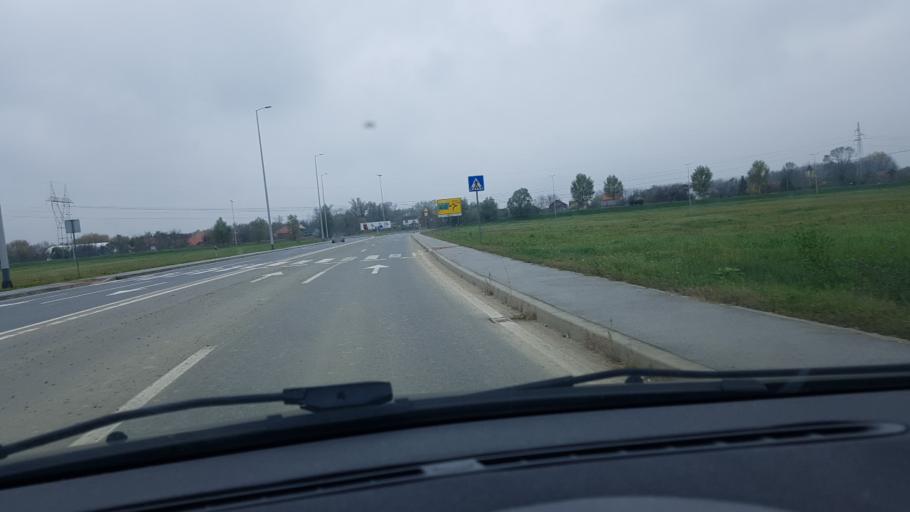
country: HR
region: Grad Zagreb
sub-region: Sesvete
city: Sesvete
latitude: 45.7946
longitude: 16.1480
